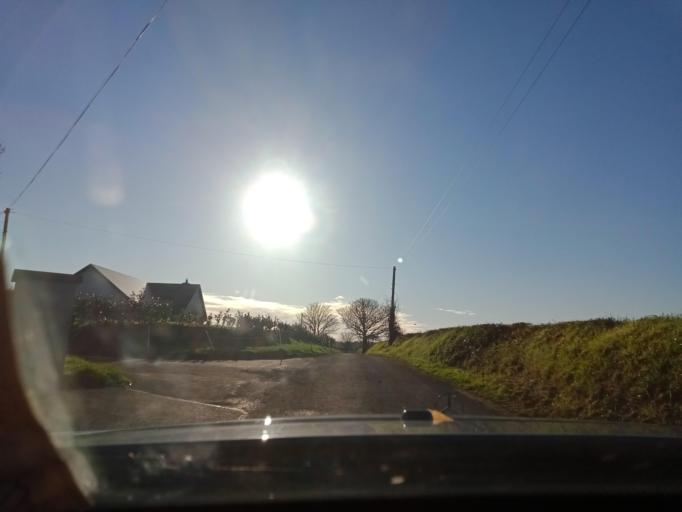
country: IE
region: Leinster
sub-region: Kilkenny
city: Mooncoin
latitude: 52.3094
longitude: -7.2268
